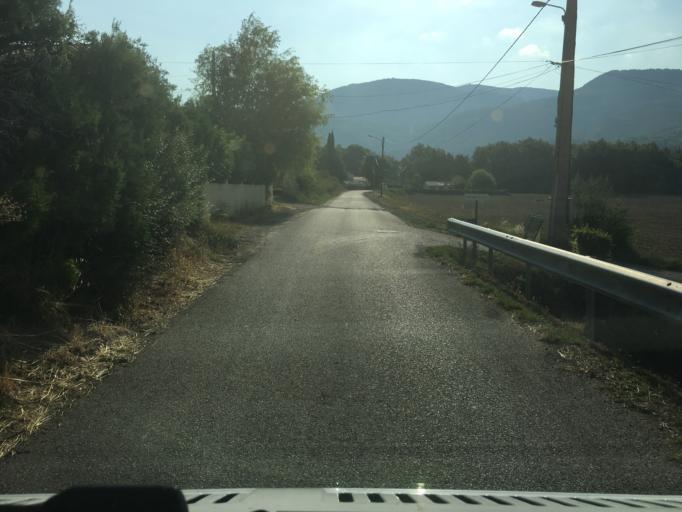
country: FR
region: Provence-Alpes-Cote d'Azur
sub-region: Departement des Alpes-de-Haute-Provence
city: Mallemoisson
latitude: 43.9413
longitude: 6.1770
